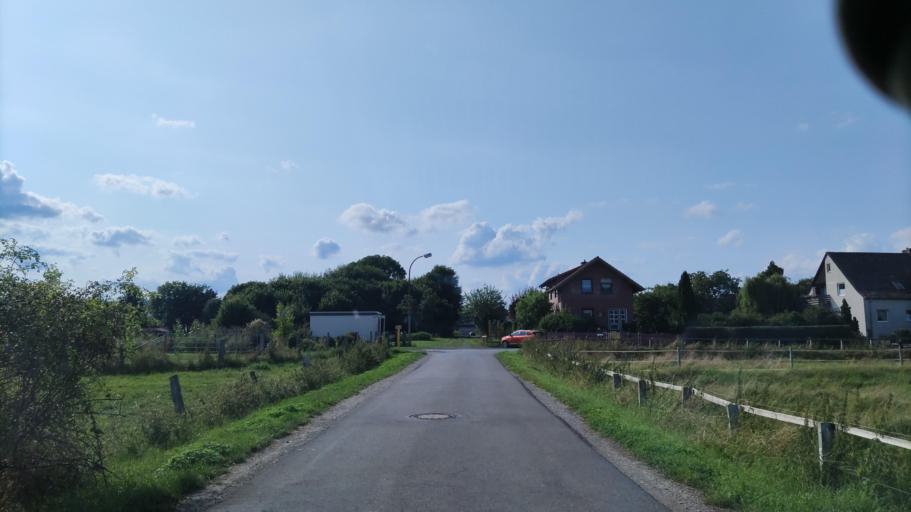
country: DE
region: Lower Saxony
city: Moringen
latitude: 51.7002
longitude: 9.8793
